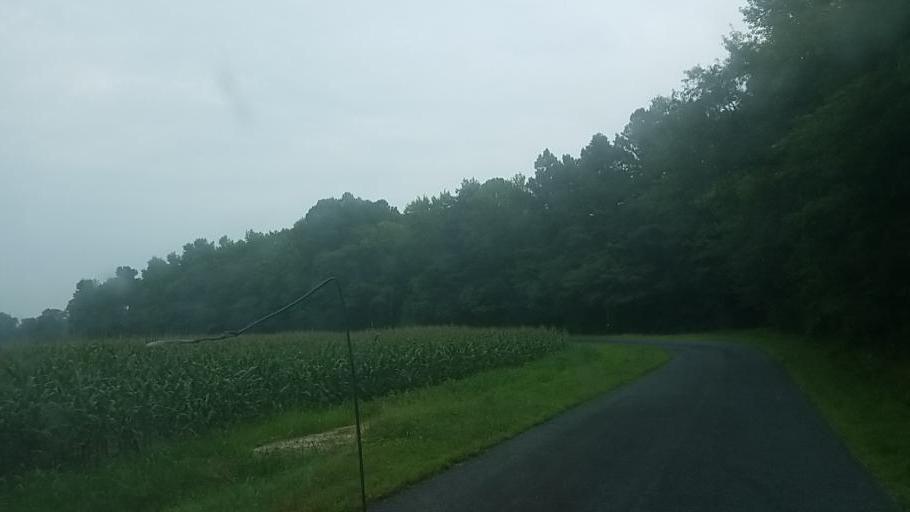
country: US
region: Delaware
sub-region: Sussex County
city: Selbyville
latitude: 38.4352
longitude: -75.2861
